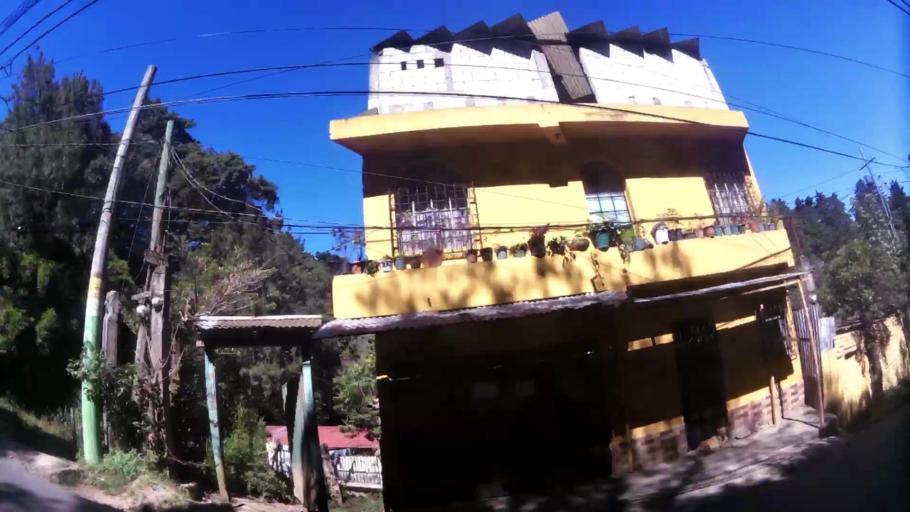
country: GT
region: Guatemala
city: San Jose Pinula
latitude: 14.5397
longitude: -90.4152
